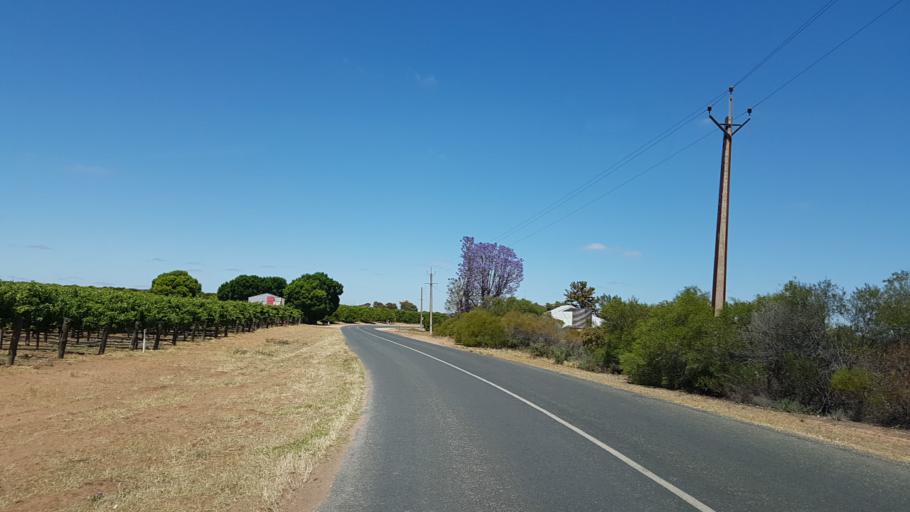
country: AU
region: South Australia
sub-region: Loxton Waikerie
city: Waikerie
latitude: -34.1729
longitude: 140.0307
